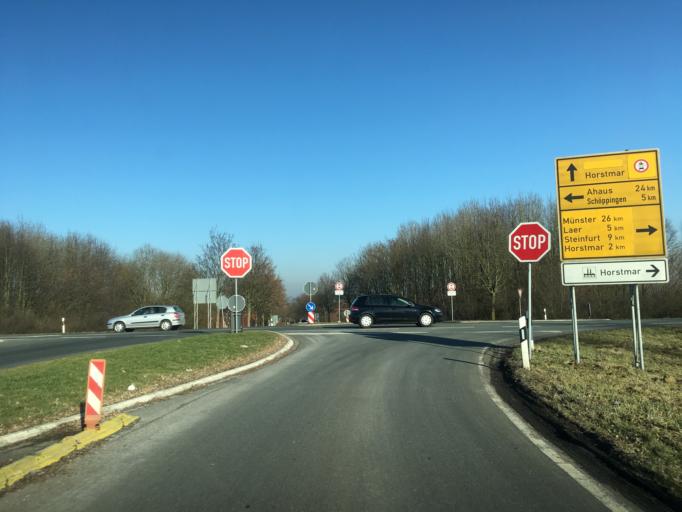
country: DE
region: North Rhine-Westphalia
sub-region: Regierungsbezirk Munster
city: Horstmar
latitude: 52.0776
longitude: 7.2944
